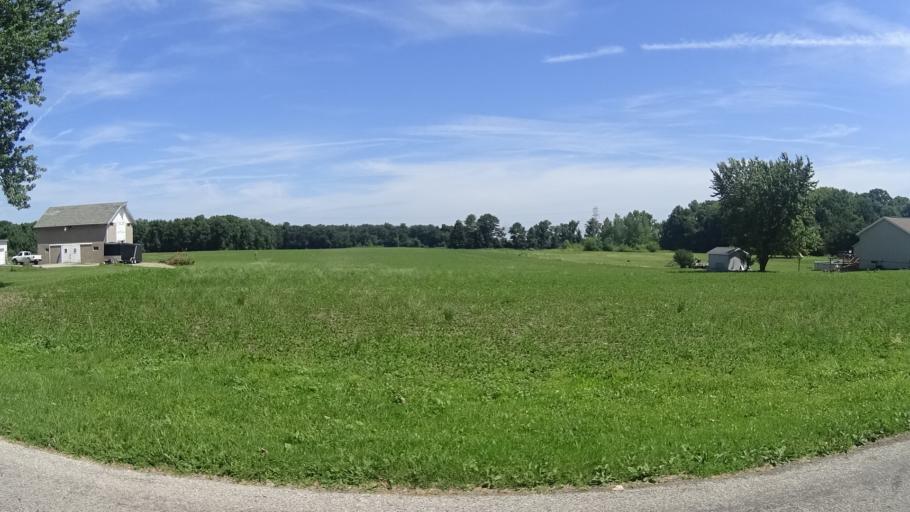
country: US
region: Ohio
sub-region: Lorain County
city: Vermilion
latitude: 41.3547
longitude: -82.4445
